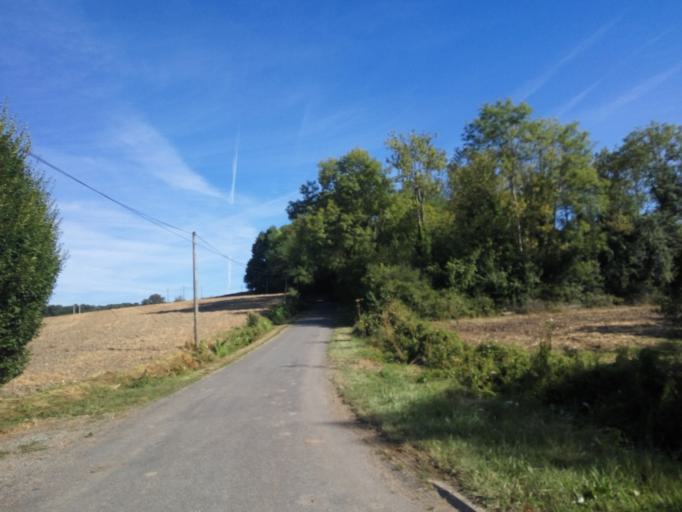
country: FR
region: Auvergne
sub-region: Departement de l'Allier
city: Brugheas
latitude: 46.0945
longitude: 3.3577
